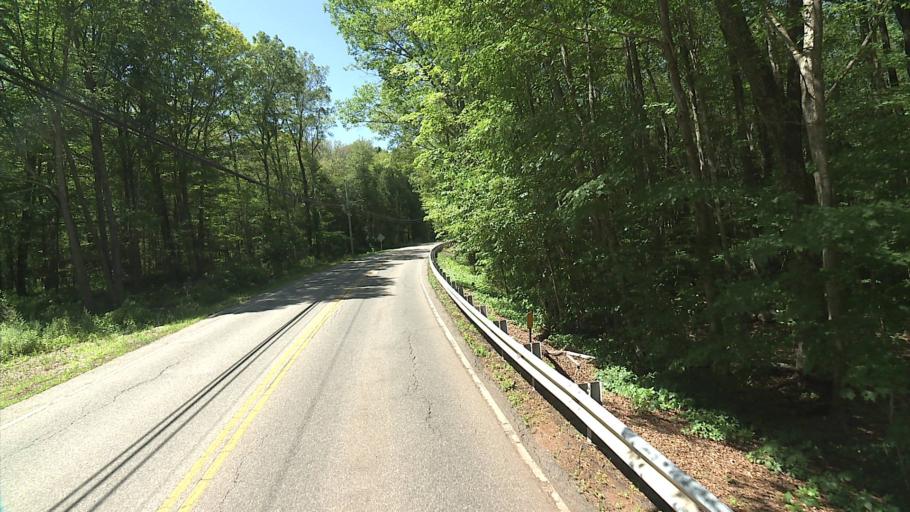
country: US
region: Connecticut
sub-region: New London County
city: Colchester
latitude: 41.5901
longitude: -72.3048
